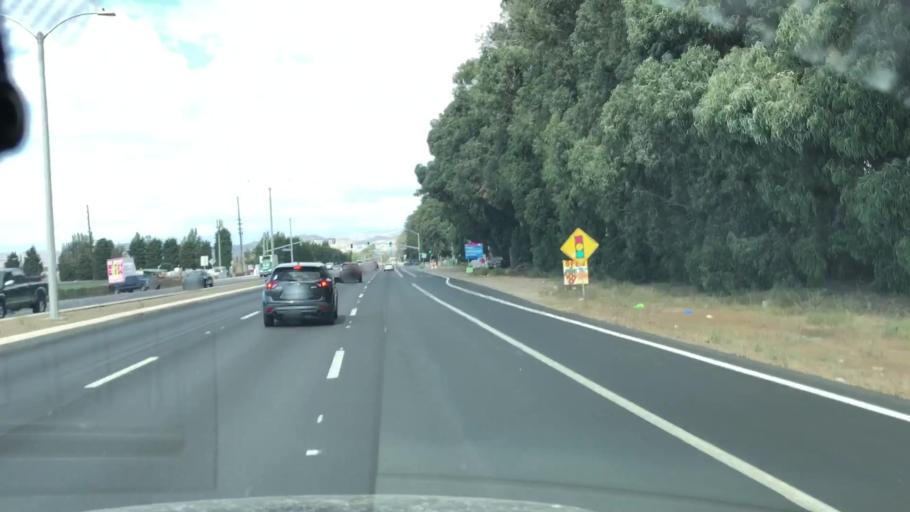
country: US
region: California
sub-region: Ventura County
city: Oxnard Shores
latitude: 34.2176
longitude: -119.2210
